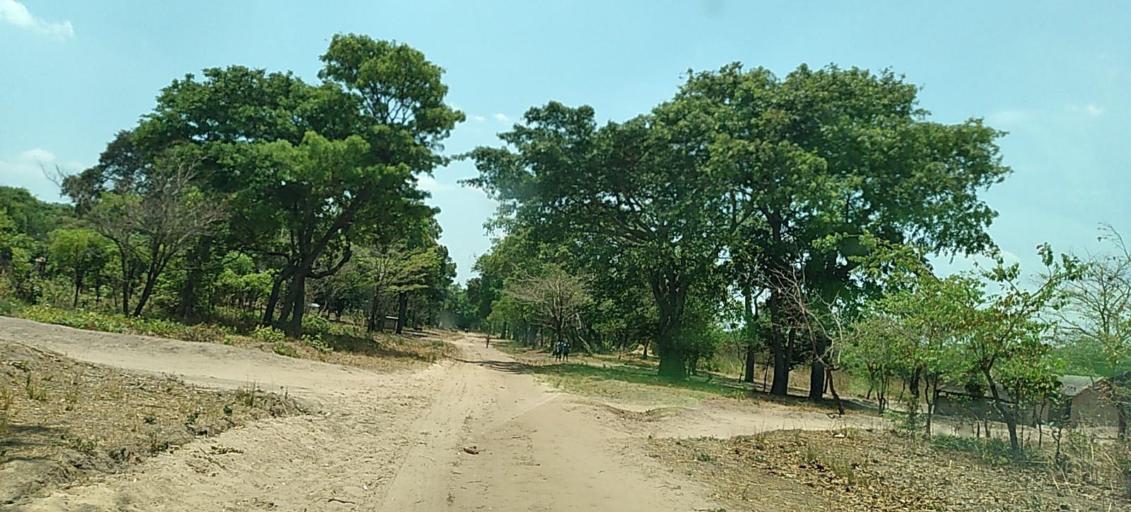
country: CD
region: Katanga
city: Kolwezi
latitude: -11.3760
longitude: 25.2161
